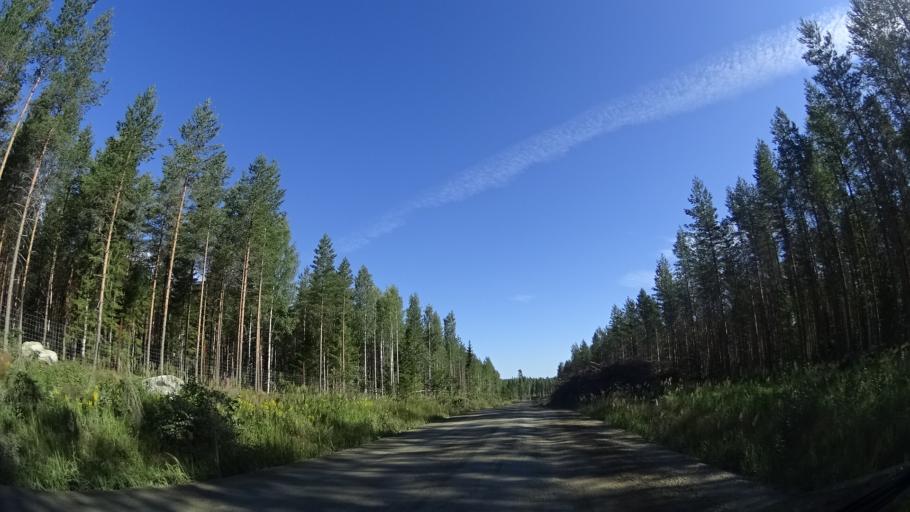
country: FI
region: Central Finland
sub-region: Jyvaeskylae
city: Petaejaevesi
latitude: 62.3102
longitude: 25.3434
